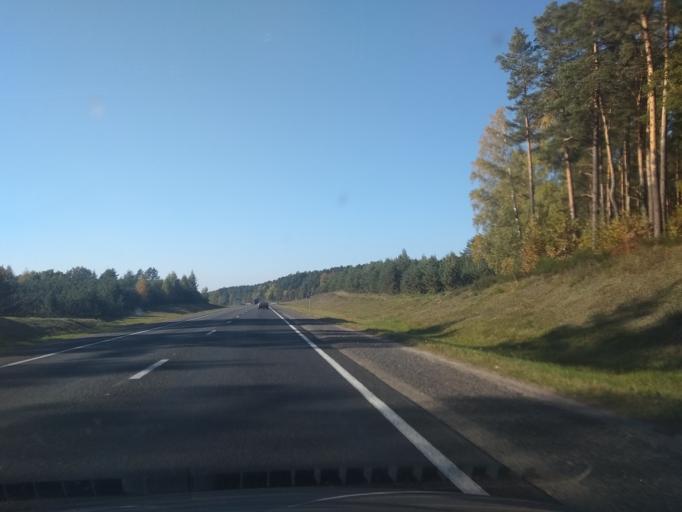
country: BY
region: Grodnenskaya
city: Zhyrovichy
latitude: 53.0498
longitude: 25.3434
